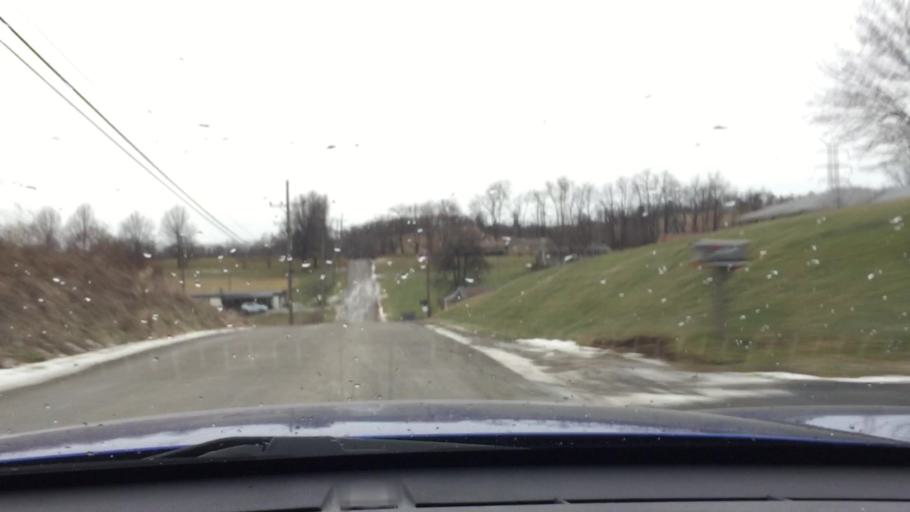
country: US
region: Pennsylvania
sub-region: Westmoreland County
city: Fellsburg
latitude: 40.1591
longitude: -79.8260
